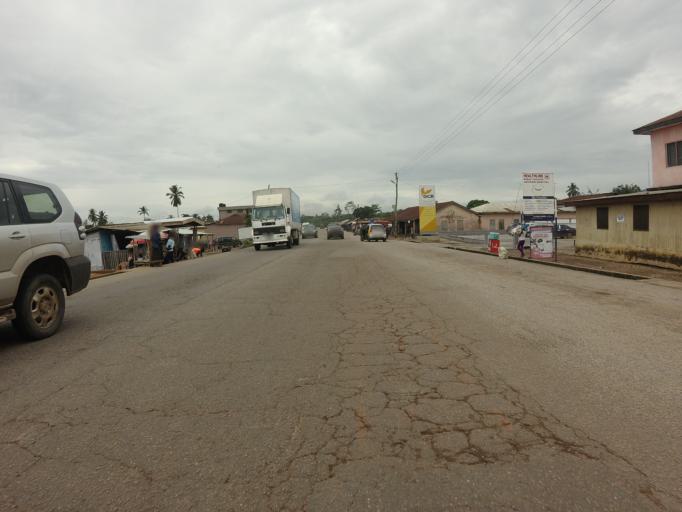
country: GH
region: Eastern
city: Begoro
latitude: 6.3834
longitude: -0.5508
